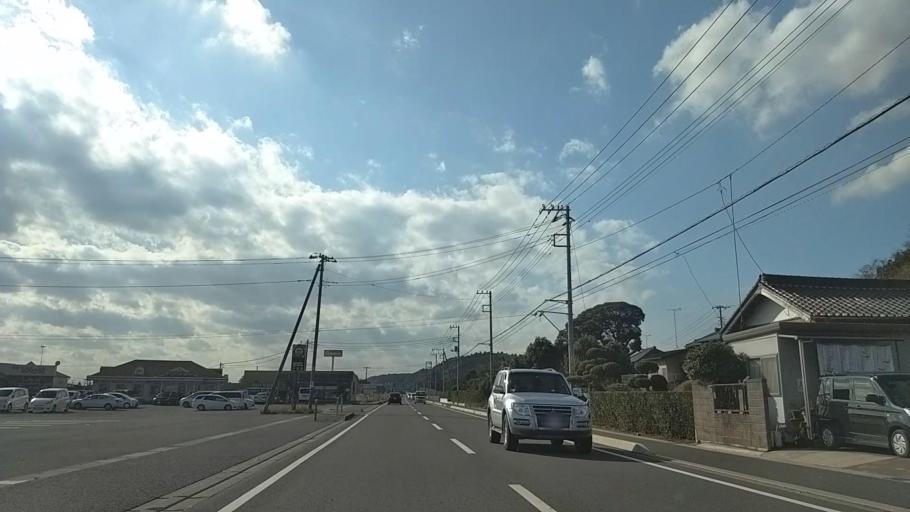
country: JP
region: Chiba
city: Naruto
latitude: 35.6273
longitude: 140.4450
